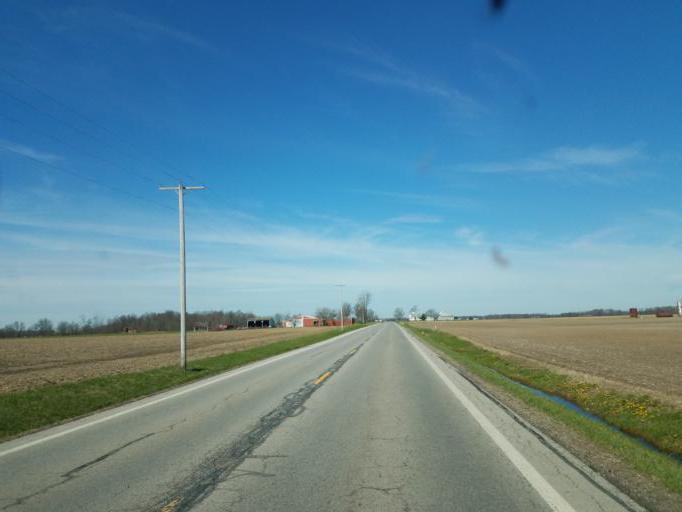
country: US
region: Ohio
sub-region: Morrow County
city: Cardington
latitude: 40.5869
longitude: -82.9253
